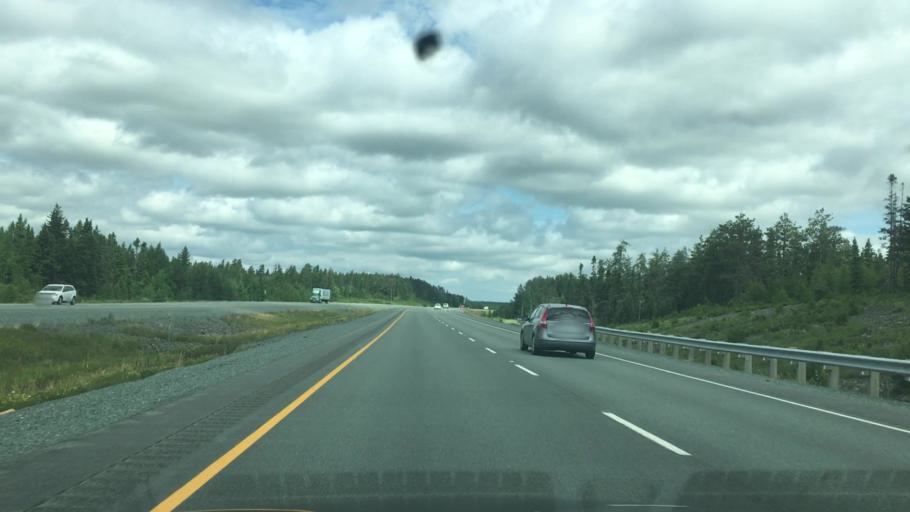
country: CA
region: Nova Scotia
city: Oxford
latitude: 45.6424
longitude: -63.7449
